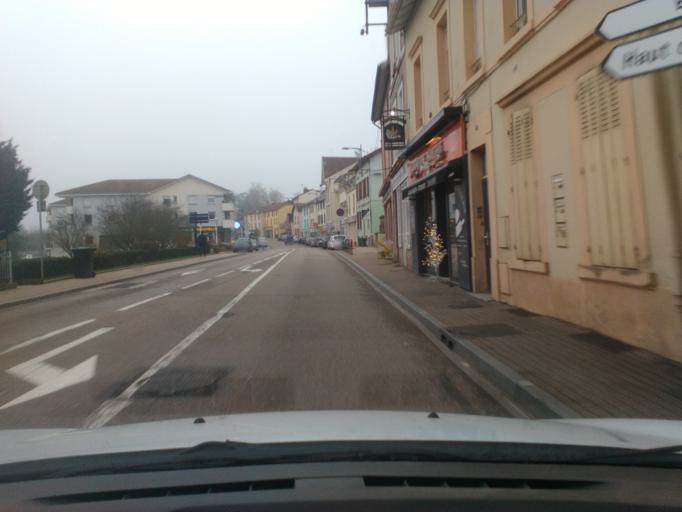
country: FR
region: Lorraine
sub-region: Departement des Vosges
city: Golbey
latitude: 48.1976
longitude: 6.4388
